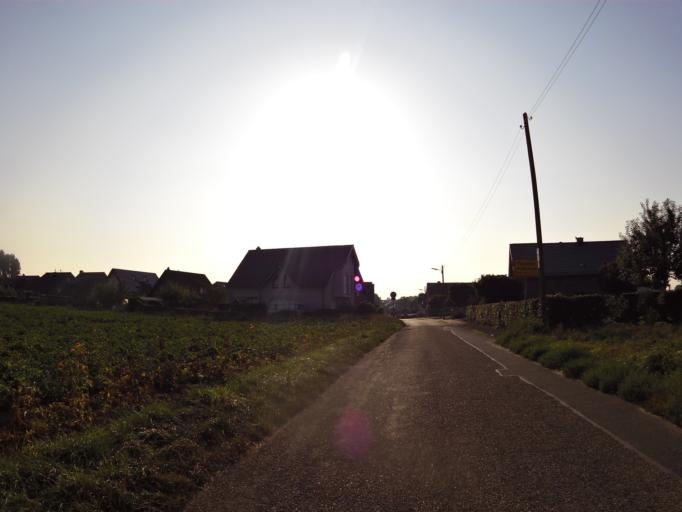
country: DE
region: North Rhine-Westphalia
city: Geilenkirchen
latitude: 50.9543
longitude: 6.0702
